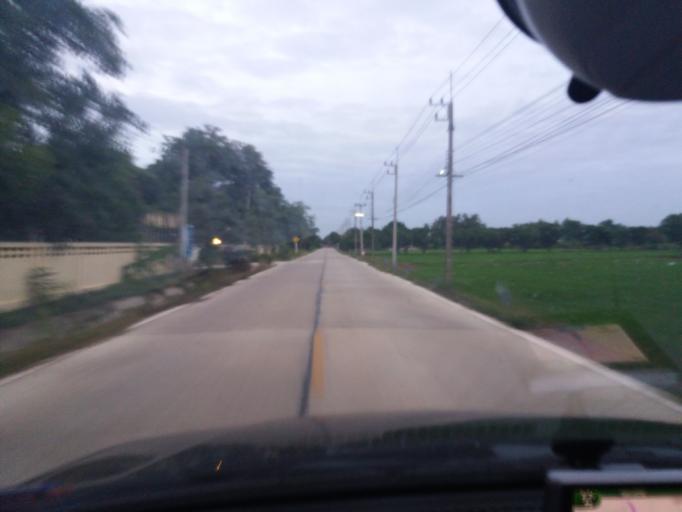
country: TH
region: Suphan Buri
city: Ban Sam Chuk
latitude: 14.7327
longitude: 100.0855
